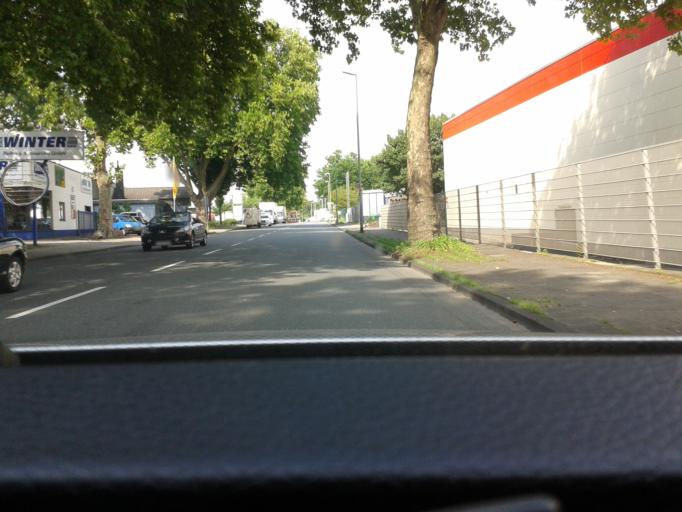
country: DE
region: North Rhine-Westphalia
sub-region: Regierungsbezirk Dusseldorf
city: Hochfeld
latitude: 51.4182
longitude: 6.6936
